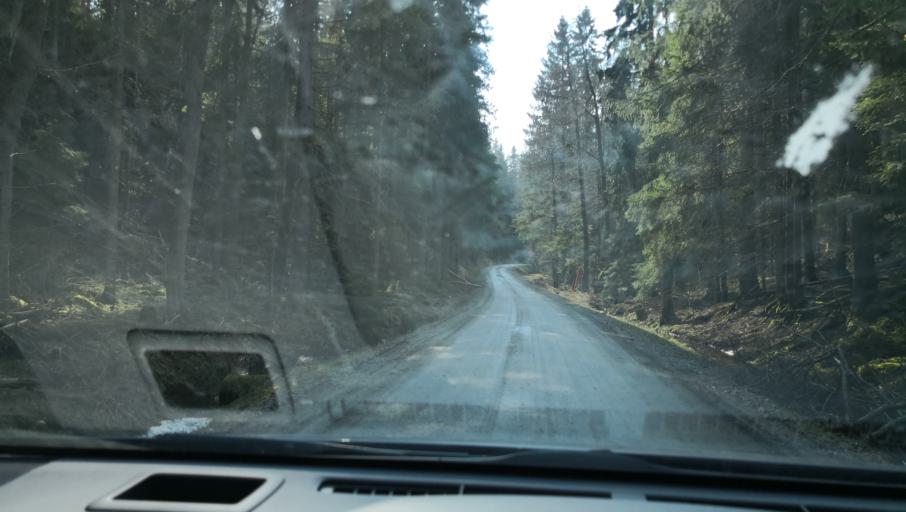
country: SE
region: OErebro
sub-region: Lindesbergs Kommun
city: Frovi
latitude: 59.3883
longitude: 15.3947
